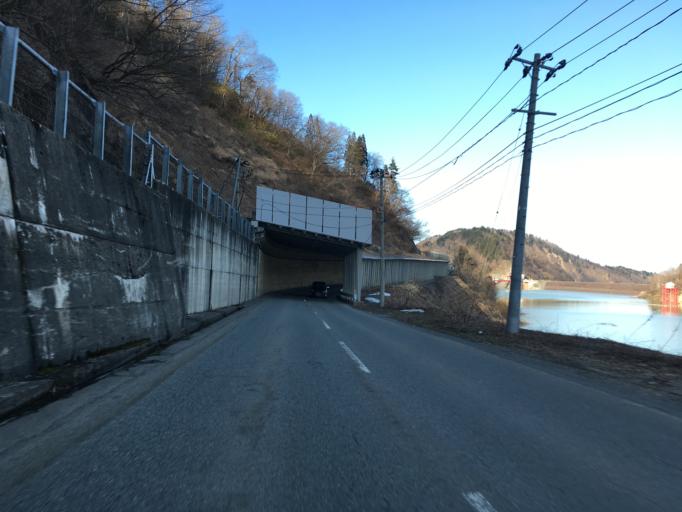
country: JP
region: Yamagata
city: Nagai
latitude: 37.9670
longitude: 139.9134
